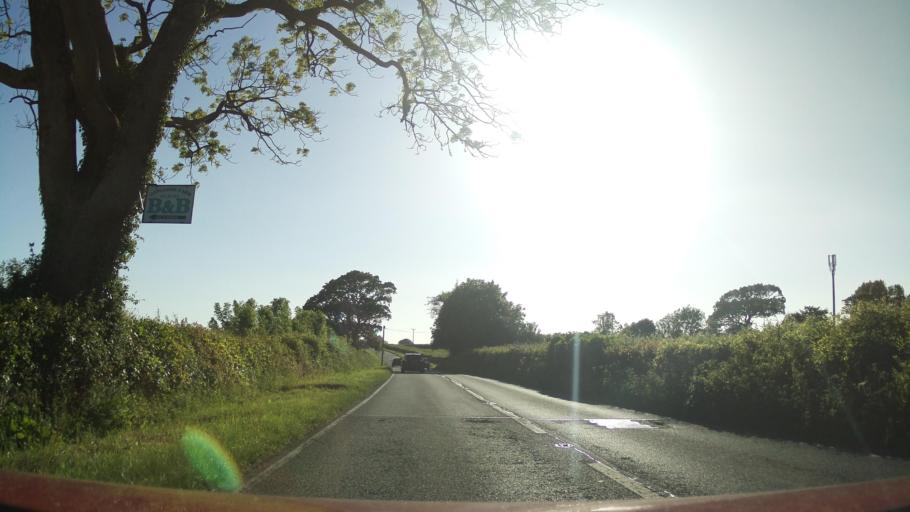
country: GB
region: England
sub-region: Devon
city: Colyton
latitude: 50.7182
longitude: -3.1034
